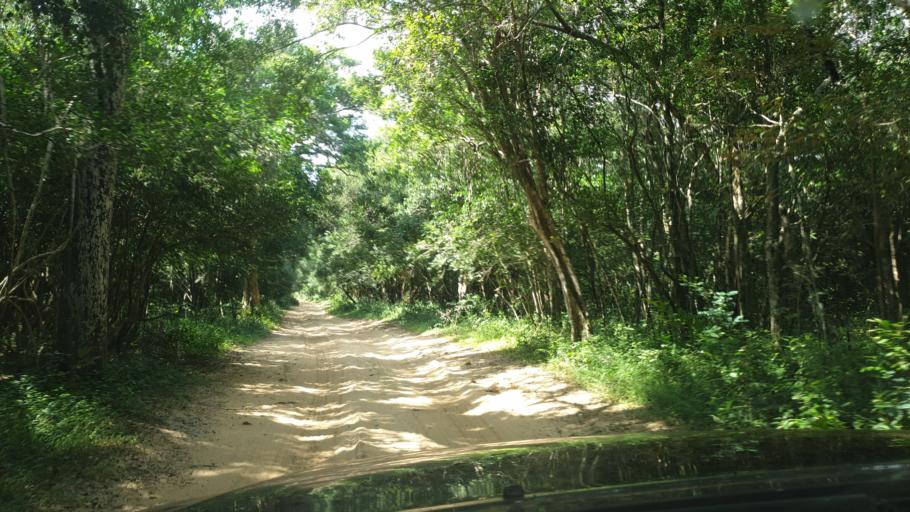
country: LK
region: North Central
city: Anuradhapura
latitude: 8.4176
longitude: 80.0225
